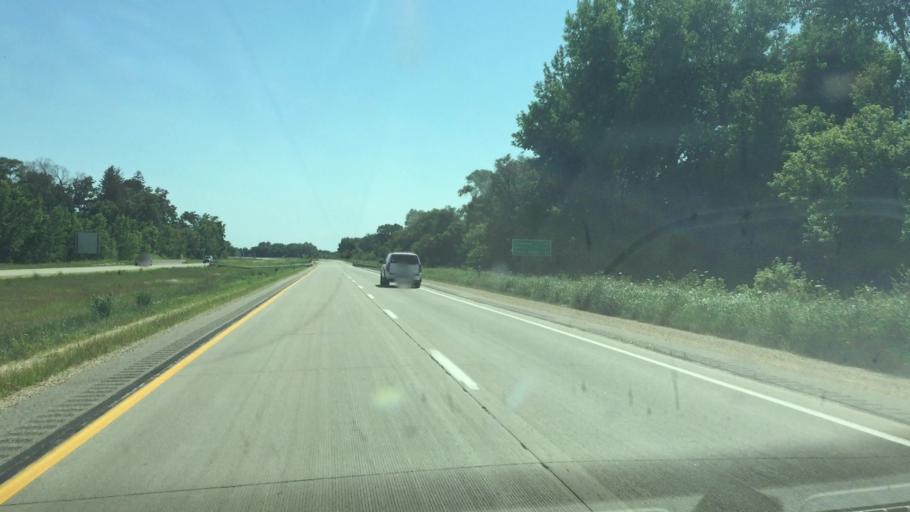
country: US
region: Iowa
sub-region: Jones County
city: Monticello
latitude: 42.2022
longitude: -91.2059
